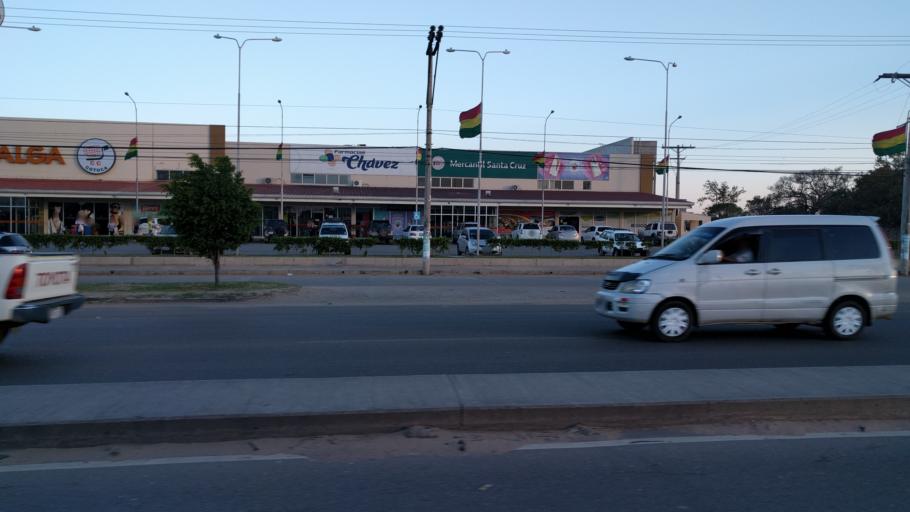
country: BO
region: Santa Cruz
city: Cotoca
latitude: -17.7652
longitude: -63.1047
